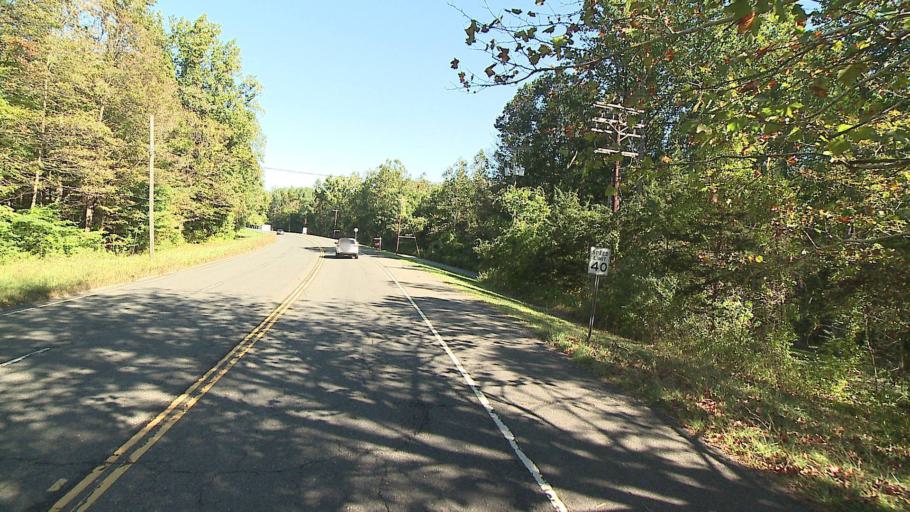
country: US
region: Connecticut
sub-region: Fairfield County
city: Danbury
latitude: 41.4740
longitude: -73.4072
